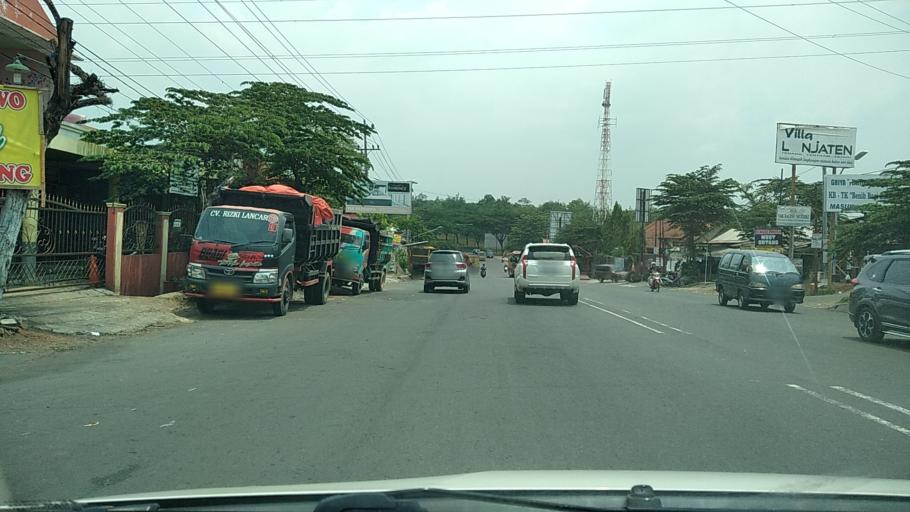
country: ID
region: Central Java
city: Semarang
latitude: -7.0220
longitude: 110.3361
